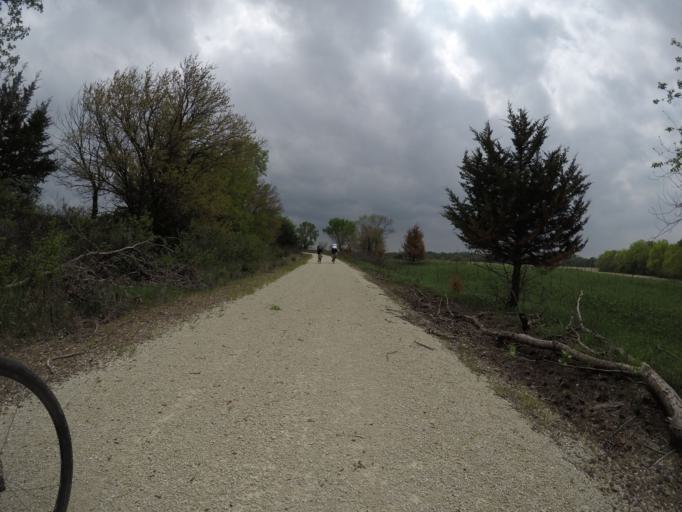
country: US
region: Nebraska
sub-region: Gage County
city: Wymore
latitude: 40.1922
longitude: -96.6656
